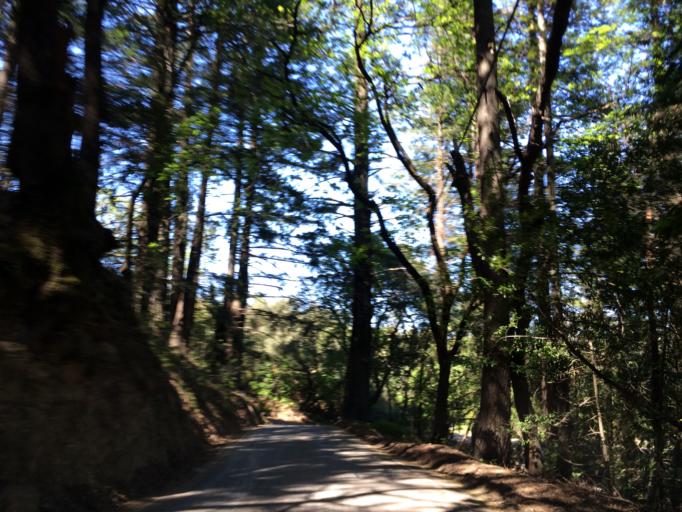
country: US
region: California
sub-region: Santa Clara County
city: Monte Sereno
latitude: 37.1877
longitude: -122.0315
